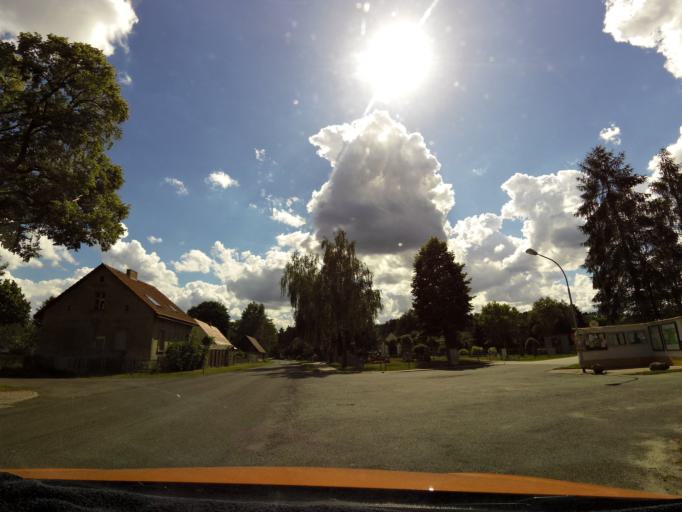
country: DE
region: Brandenburg
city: Erkner
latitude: 52.3146
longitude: 13.7490
